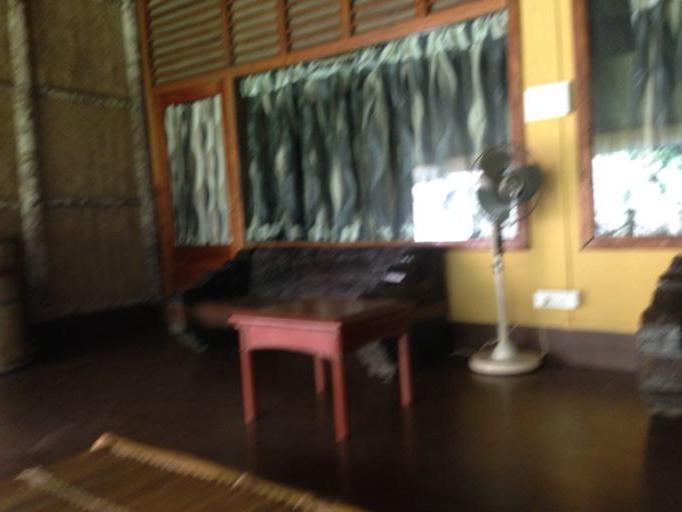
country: IN
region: Karnataka
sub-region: Belgaum
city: Belgaum
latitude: 15.8219
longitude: 74.4799
